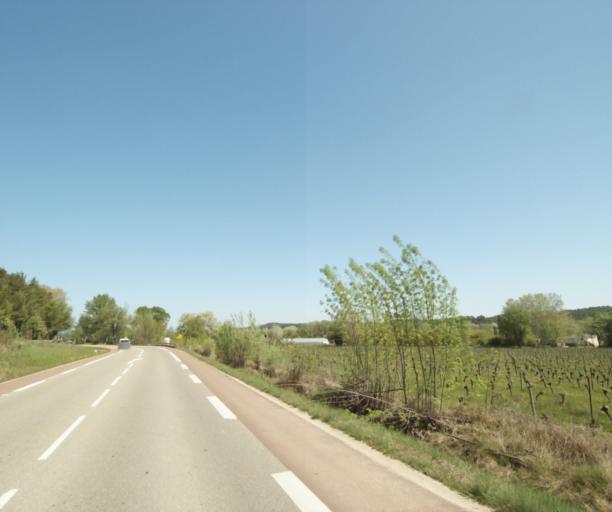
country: FR
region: Languedoc-Roussillon
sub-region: Departement de l'Herault
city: Montferrier-sur-Lez
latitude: 43.6802
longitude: 3.8568
